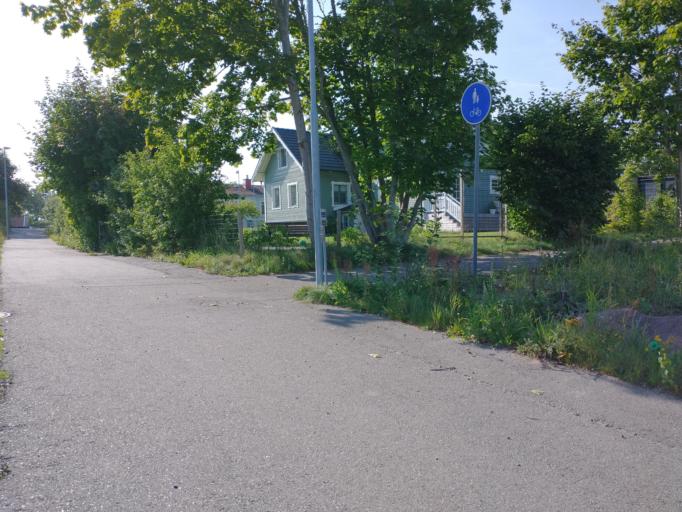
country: SE
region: Kalmar
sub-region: Kalmar Kommun
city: Lindsdal
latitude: 56.7822
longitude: 16.2895
